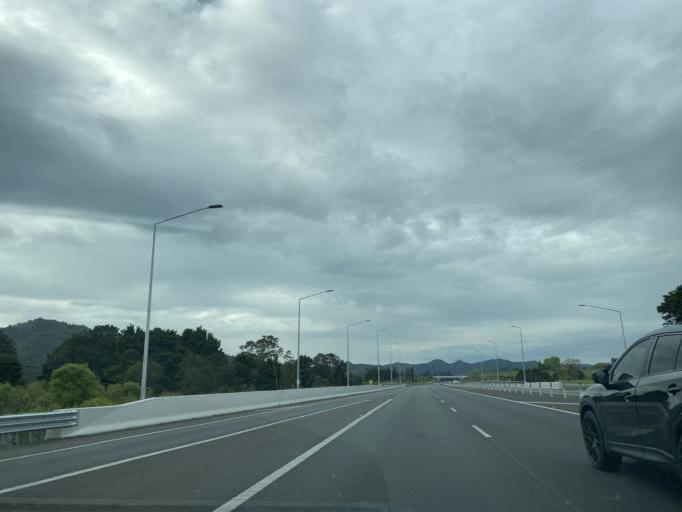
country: NZ
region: Waikato
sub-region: Waikato District
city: Ngaruawahia
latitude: -37.6194
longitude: 175.2052
